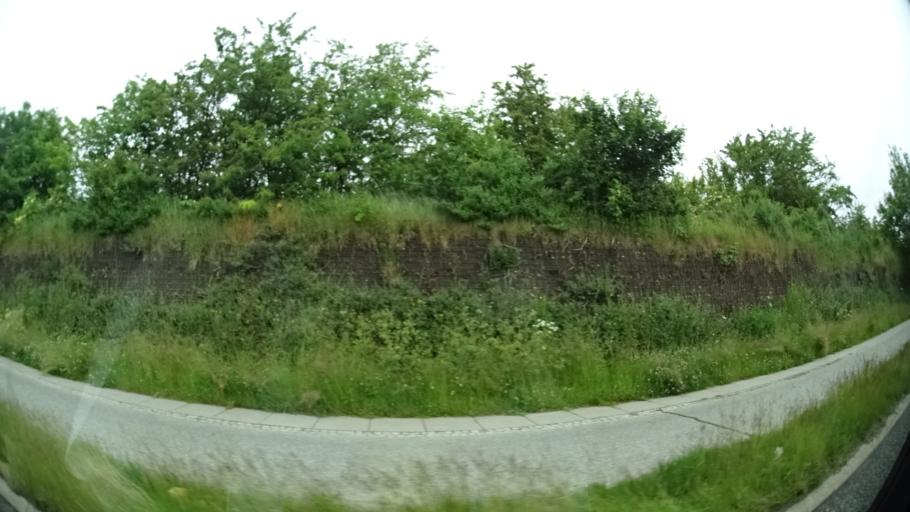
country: DK
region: Central Jutland
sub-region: Arhus Kommune
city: Arhus
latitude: 56.1749
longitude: 10.1705
